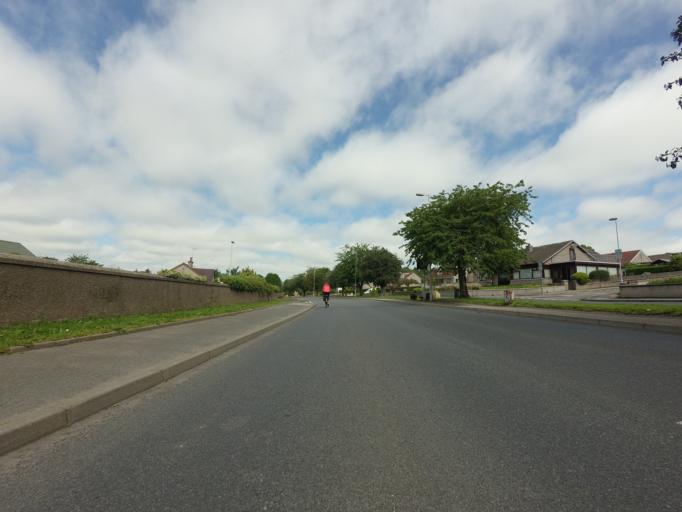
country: GB
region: Scotland
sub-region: Aberdeenshire
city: Turriff
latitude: 57.5414
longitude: -2.4720
